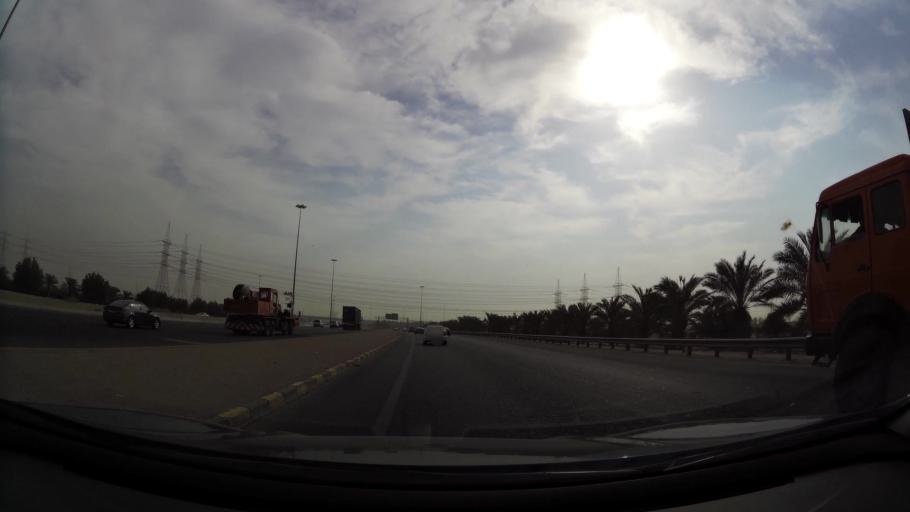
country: KW
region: Muhafazat al Jahra'
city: Al Jahra'
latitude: 29.3118
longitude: 47.7774
